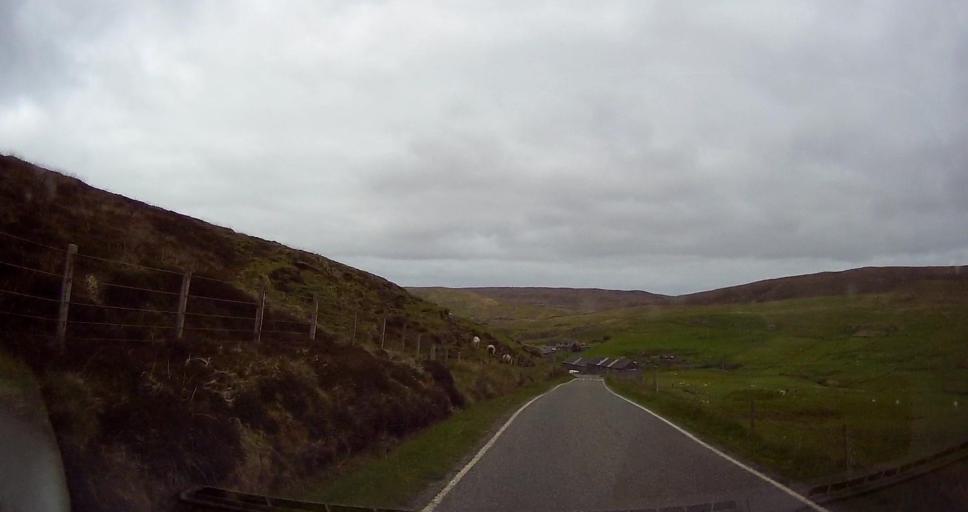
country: GB
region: Scotland
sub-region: Shetland Islands
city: Lerwick
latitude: 60.3432
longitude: -1.2775
